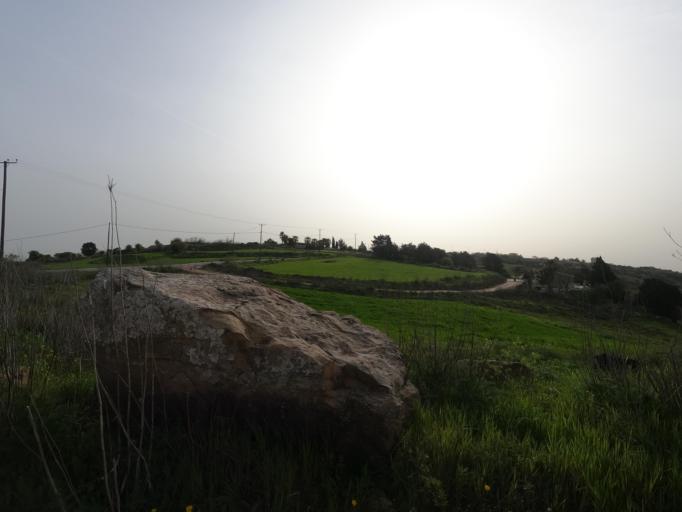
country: CY
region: Pafos
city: Pegeia
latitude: 34.9639
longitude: 32.3807
